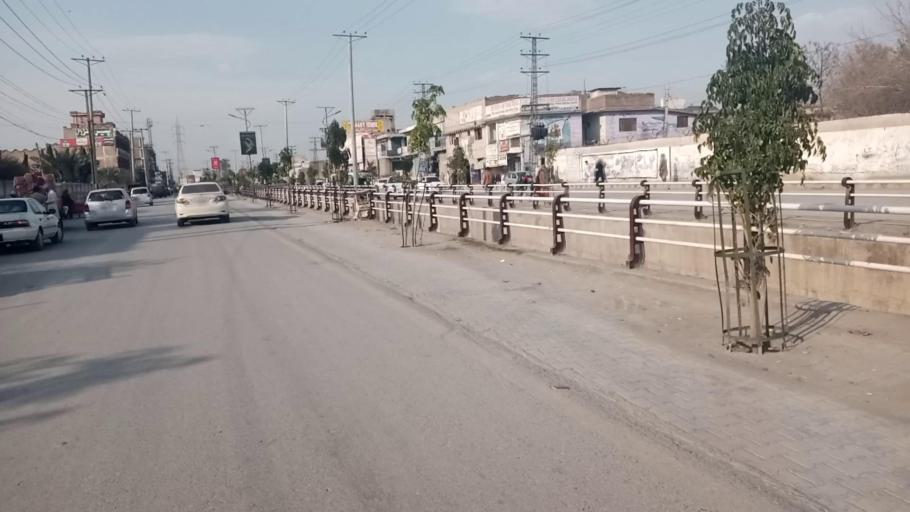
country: PK
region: Khyber Pakhtunkhwa
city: Peshawar
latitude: 33.9991
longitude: 71.4691
